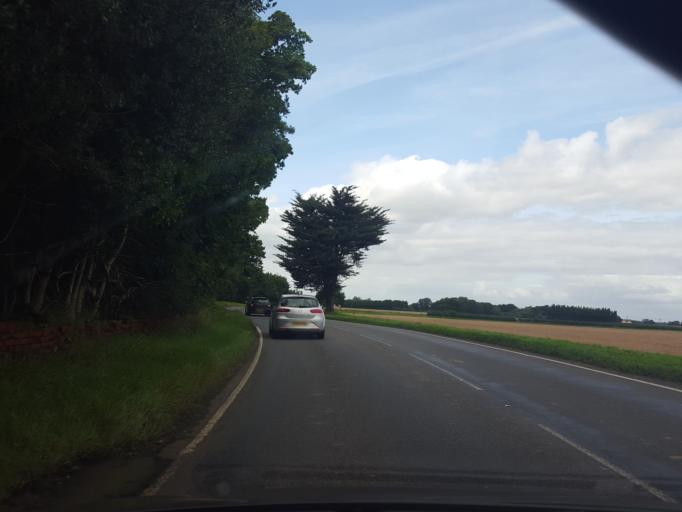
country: GB
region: England
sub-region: Essex
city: Mistley
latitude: 51.9068
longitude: 1.0830
